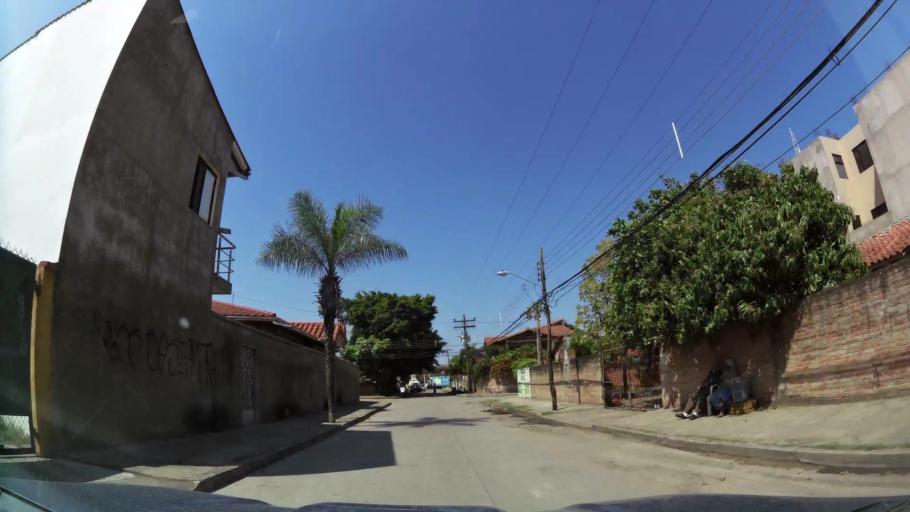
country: BO
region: Santa Cruz
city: Santa Cruz de la Sierra
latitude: -17.7512
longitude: -63.1950
